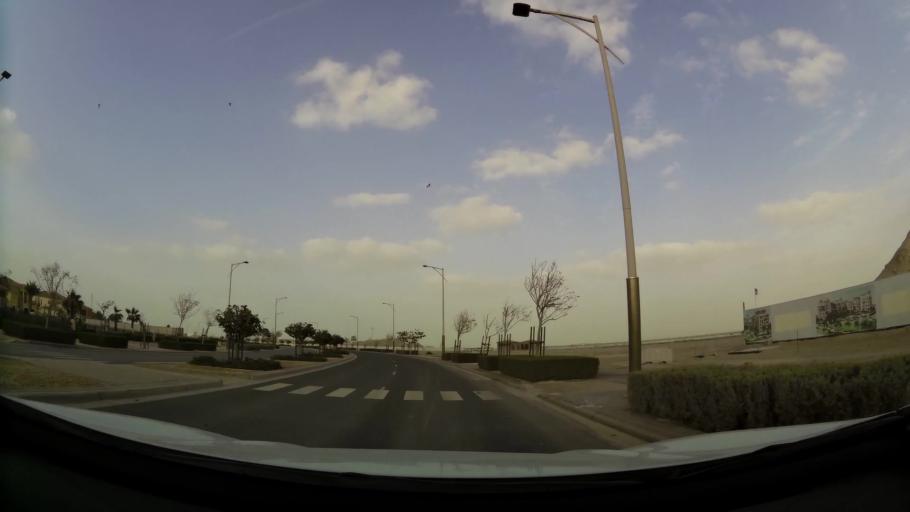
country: AE
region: Abu Dhabi
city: Abu Dhabi
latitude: 24.5575
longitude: 54.4560
